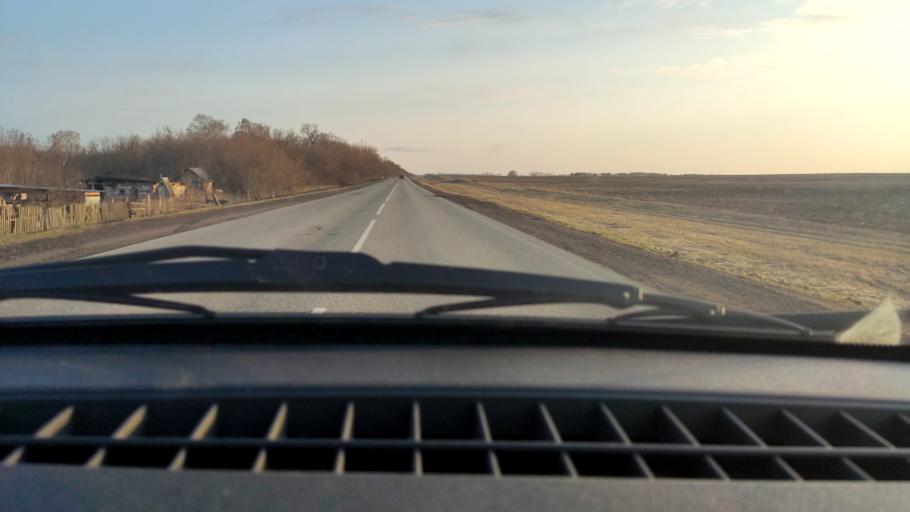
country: RU
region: Bashkortostan
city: Chishmy
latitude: 54.4792
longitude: 55.2678
